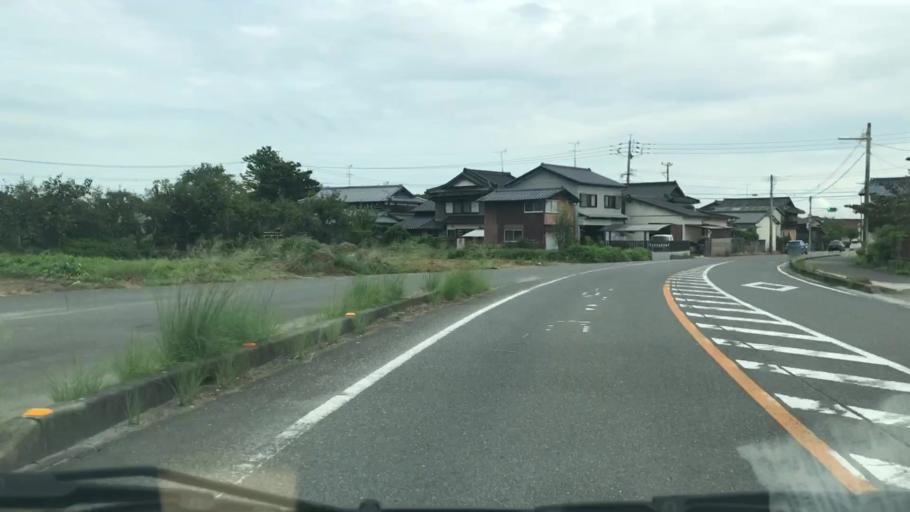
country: JP
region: Saga Prefecture
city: Saga-shi
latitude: 33.2881
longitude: 130.2497
